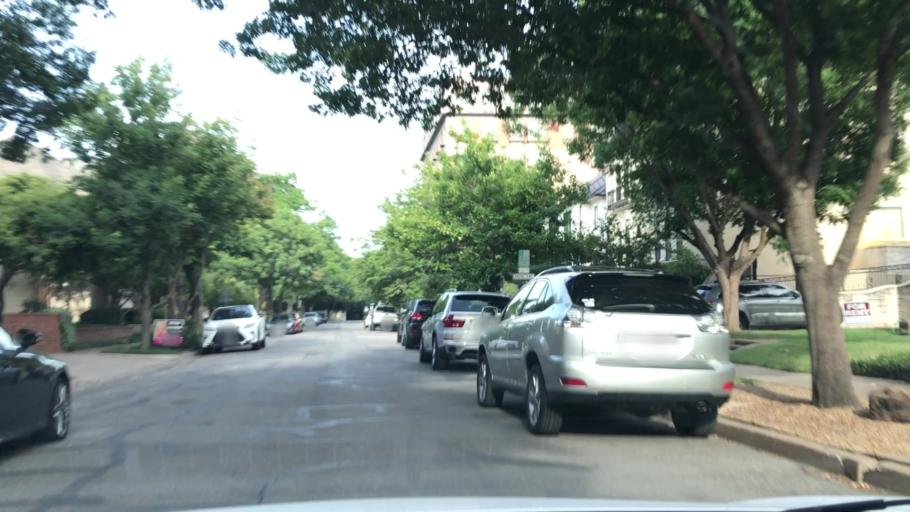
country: US
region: Texas
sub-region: Dallas County
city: Highland Park
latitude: 32.8217
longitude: -96.8043
